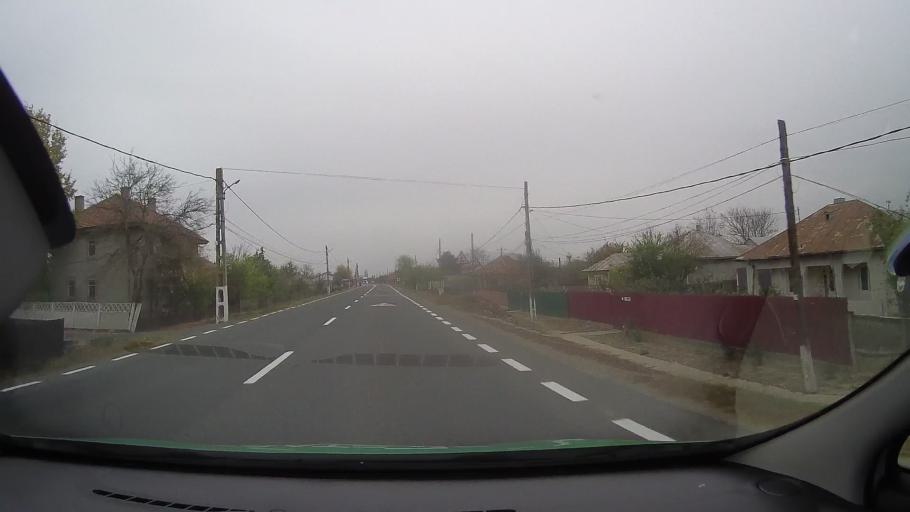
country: RO
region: Ialomita
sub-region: Comuna Giurgeni
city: Giurgeni
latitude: 44.7432
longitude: 27.8565
